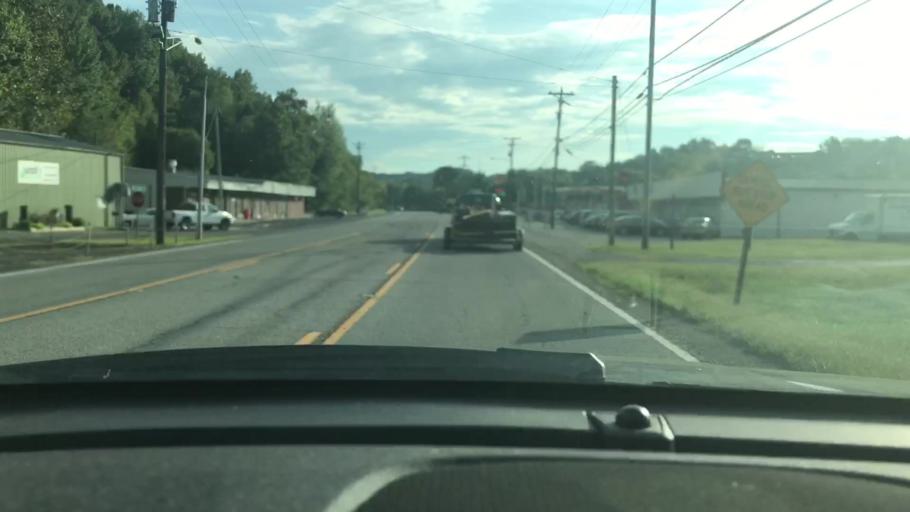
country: US
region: Tennessee
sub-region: Sumner County
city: Millersville
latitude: 36.3753
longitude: -86.7077
